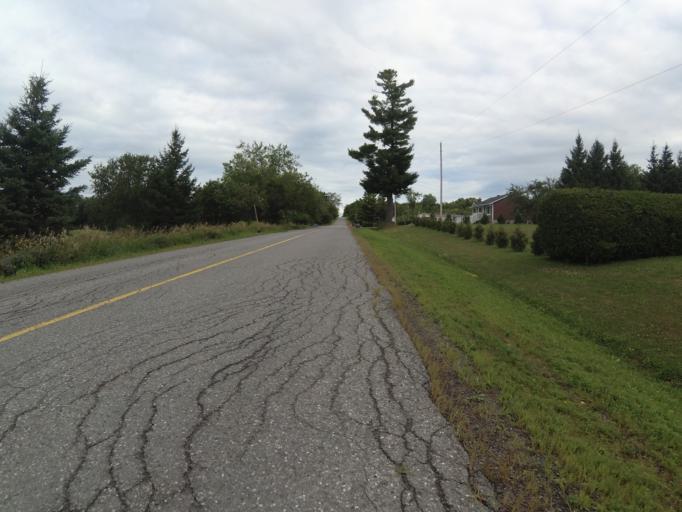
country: CA
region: Ontario
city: Clarence-Rockland
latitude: 45.4232
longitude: -75.2961
